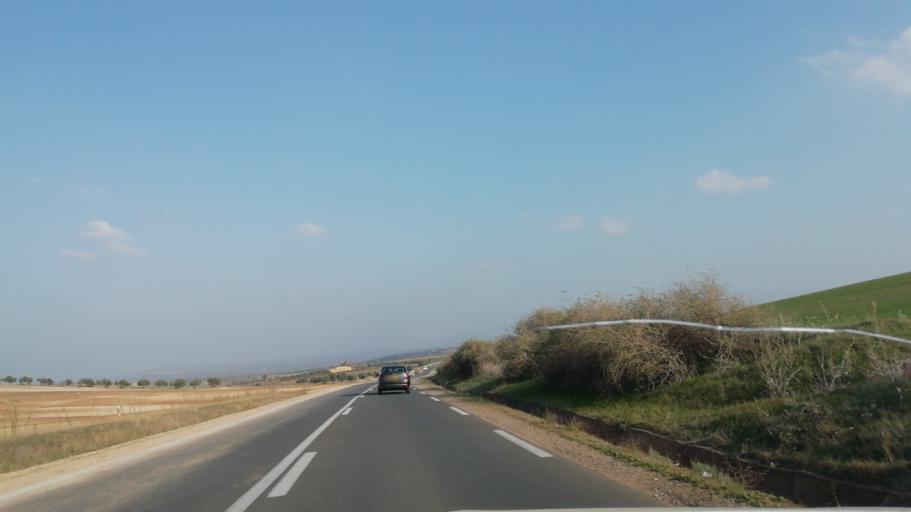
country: DZ
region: Ain Temouchent
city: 'Ain Temouchent
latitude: 35.3048
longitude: -1.0602
